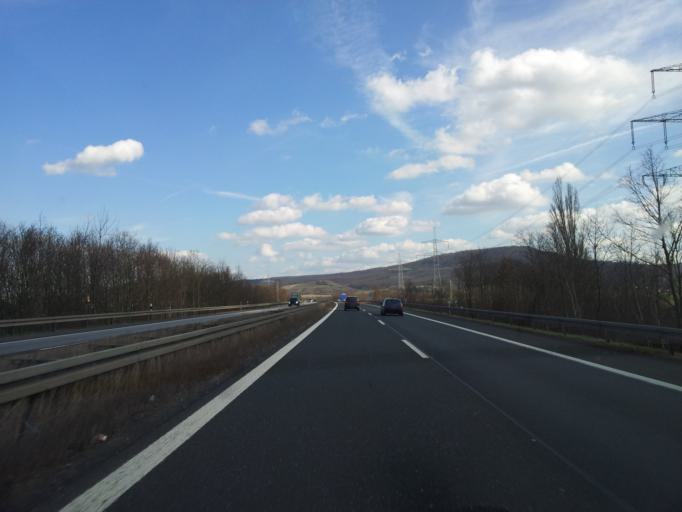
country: DE
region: Bavaria
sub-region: Regierungsbezirk Unterfranken
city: Knetzgau
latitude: 49.9817
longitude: 10.5461
